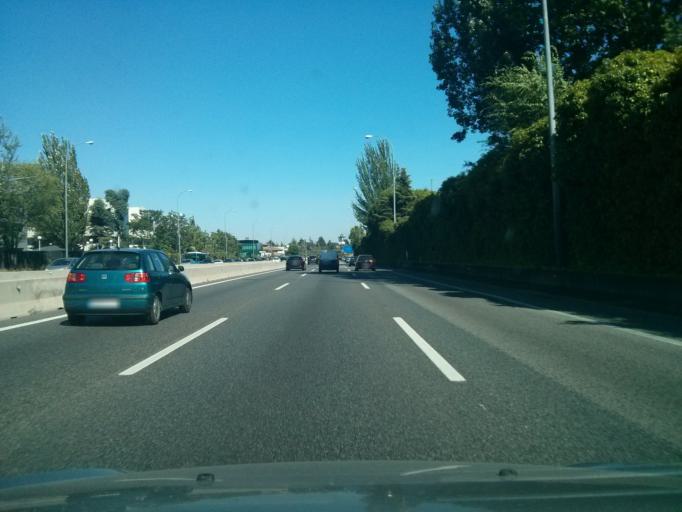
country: ES
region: Madrid
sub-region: Provincia de Madrid
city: Pozuelo de Alarcon
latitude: 40.4722
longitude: -3.8239
